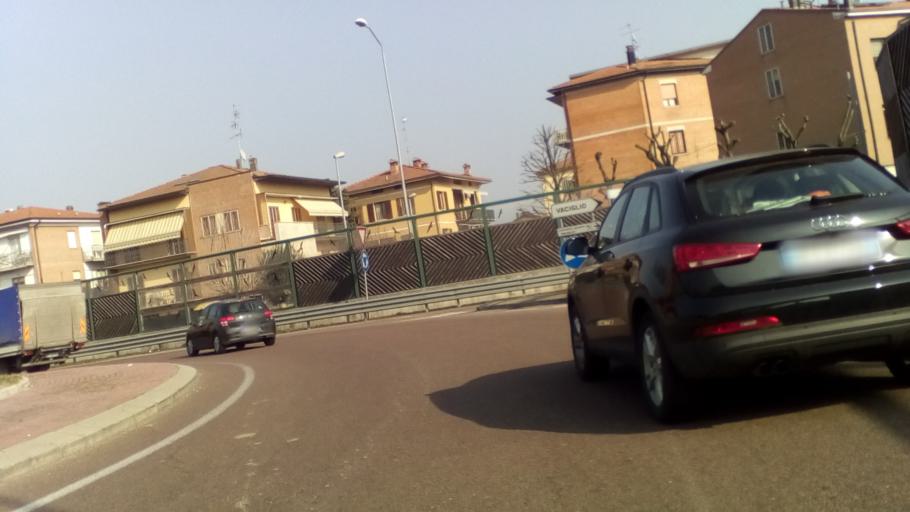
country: IT
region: Emilia-Romagna
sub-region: Provincia di Modena
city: Modena
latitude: 44.6135
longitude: 10.9368
